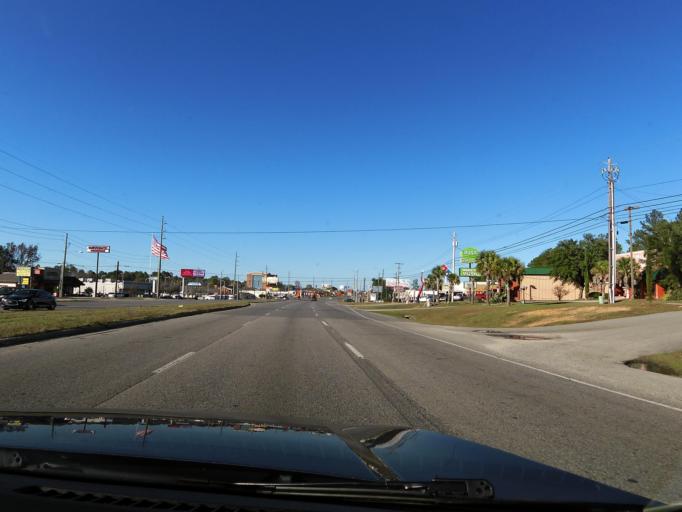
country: US
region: Alabama
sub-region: Houston County
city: Dothan
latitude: 31.2172
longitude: -85.4312
